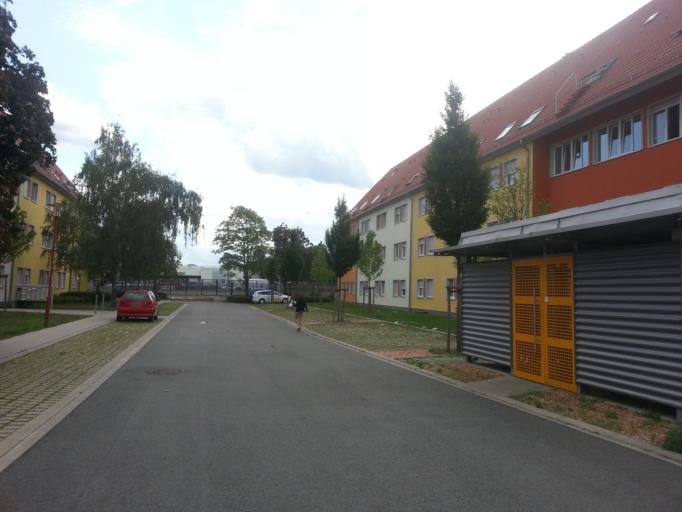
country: DE
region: Baden-Wuerttemberg
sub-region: Karlsruhe Region
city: Mannheim
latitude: 49.5091
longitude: 8.4944
